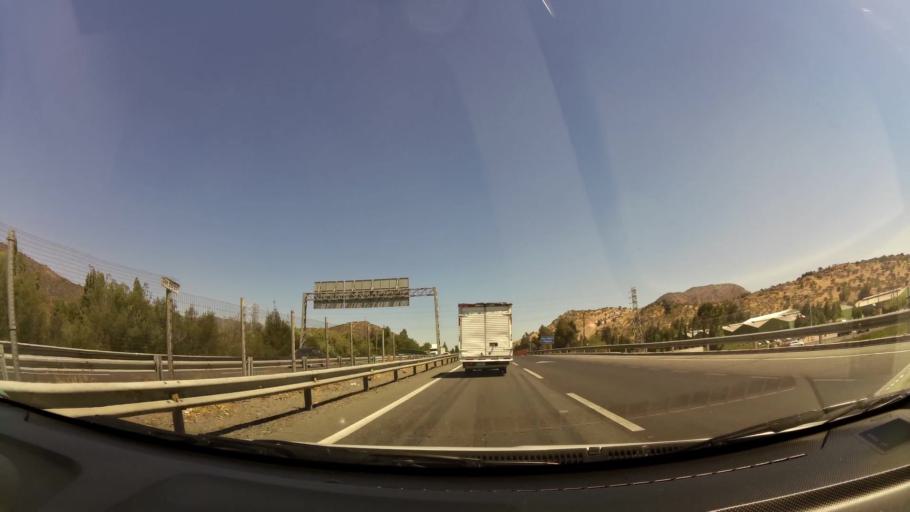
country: CL
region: O'Higgins
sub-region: Provincia de Cachapoal
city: Rengo
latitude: -34.4673
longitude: -70.8982
